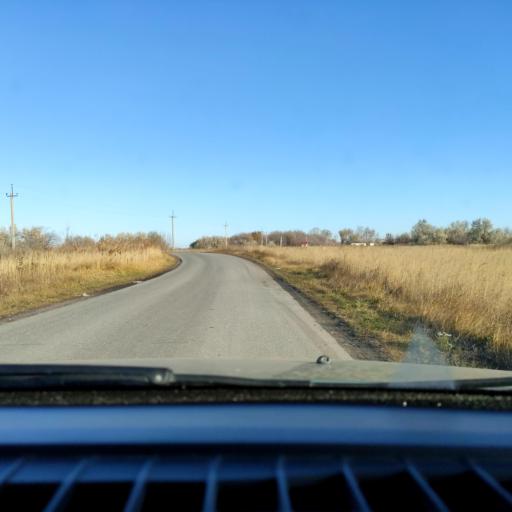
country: RU
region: Samara
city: Tol'yatti
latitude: 53.6568
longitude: 49.3315
